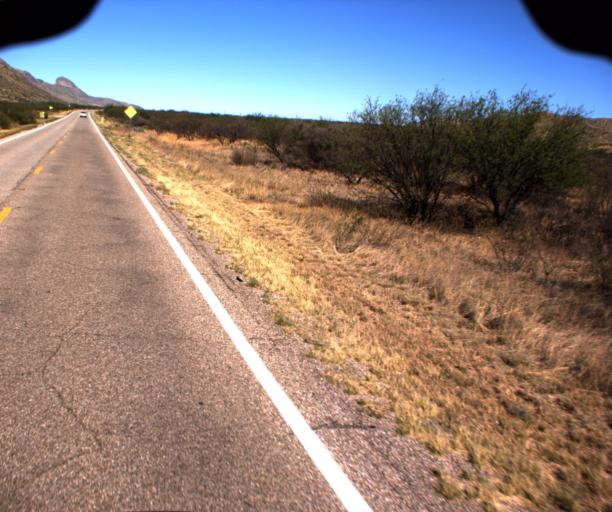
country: US
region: Arizona
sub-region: Cochise County
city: Huachuca City
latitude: 31.6943
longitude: -110.4136
